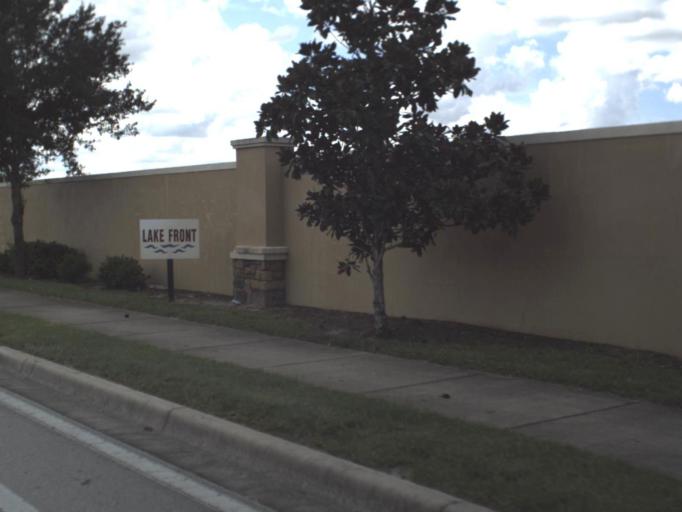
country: US
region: Florida
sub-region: Polk County
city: Jan-Phyl Village
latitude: 28.0041
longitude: -81.7680
